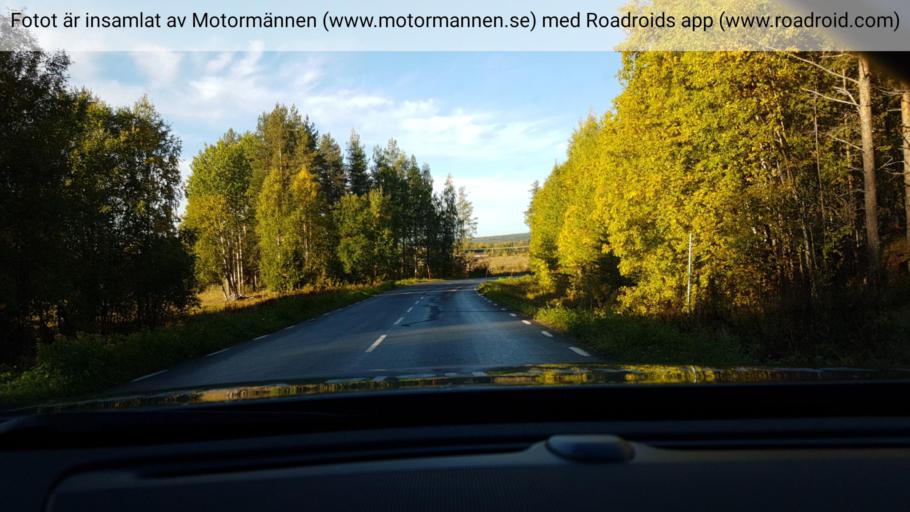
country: SE
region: Norrbotten
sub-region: Bodens Kommun
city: Boden
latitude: 65.8478
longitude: 21.7285
